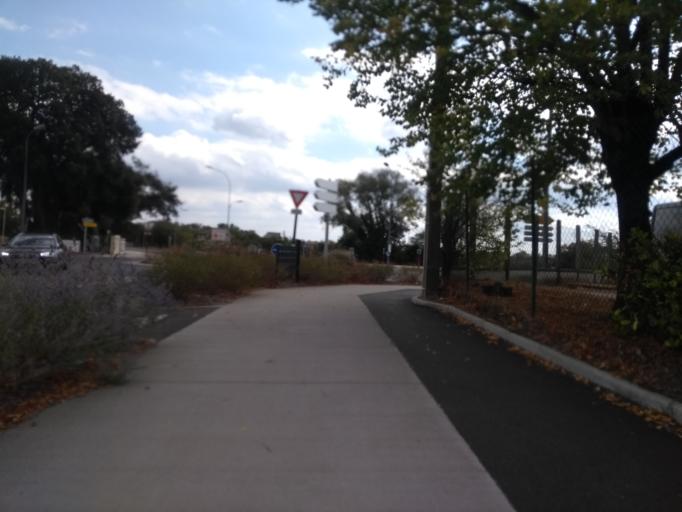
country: FR
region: Aquitaine
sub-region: Departement de la Gironde
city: Talence
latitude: 44.7967
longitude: -0.5797
